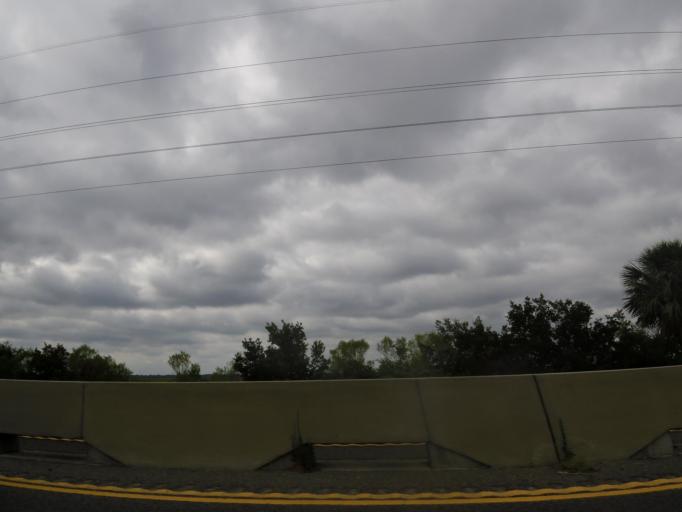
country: US
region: Georgia
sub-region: Glynn County
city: Saint Simon Mills
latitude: 31.1701
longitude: -81.4338
